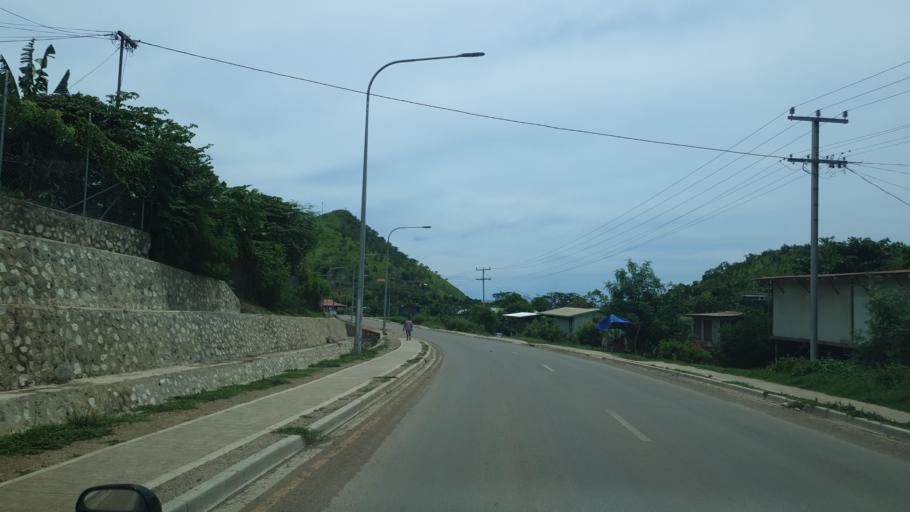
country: PG
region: National Capital
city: Port Moresby
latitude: -9.5228
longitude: 147.2410
